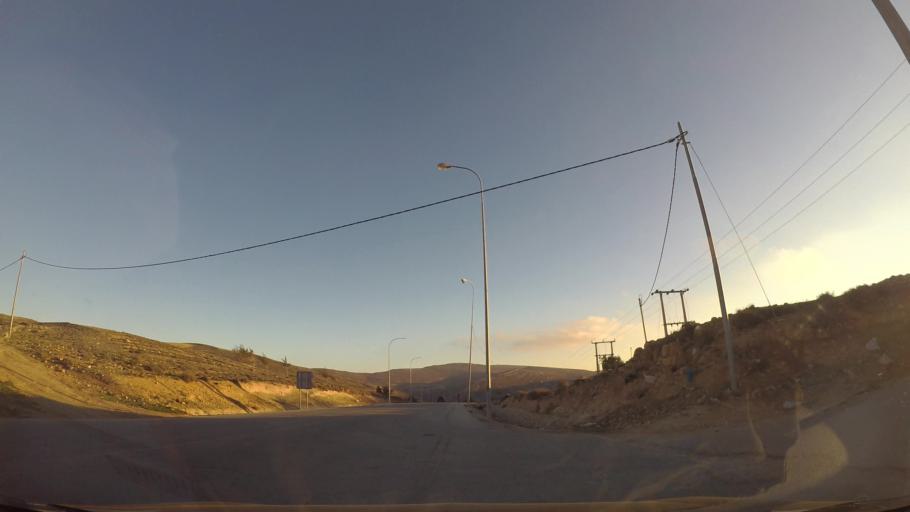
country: JO
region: Ma'an
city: Petra
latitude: 30.4025
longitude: 35.5034
